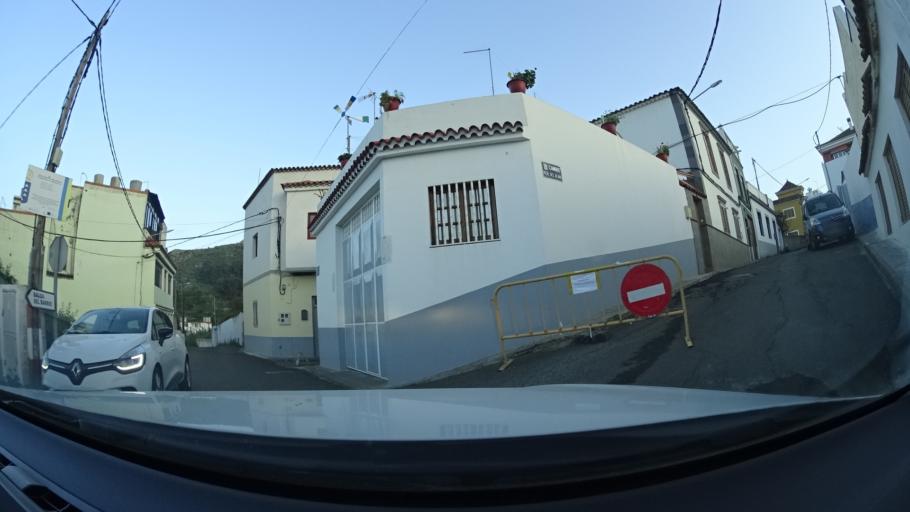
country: ES
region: Canary Islands
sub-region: Provincia de Las Palmas
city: Teror
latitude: 28.0572
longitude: -15.5435
